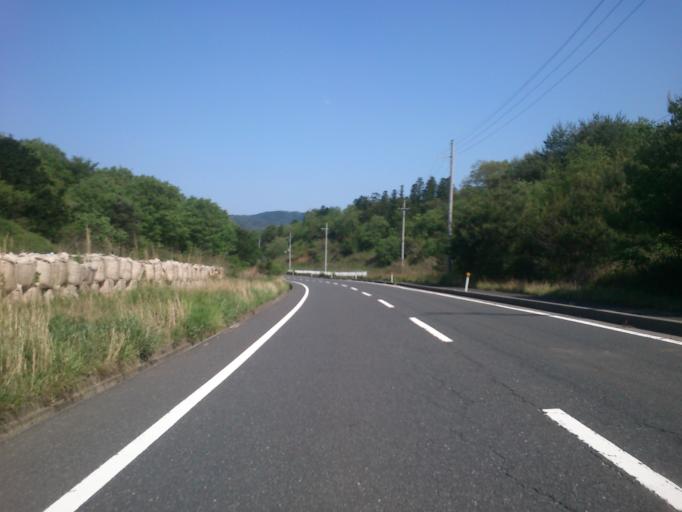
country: JP
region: Kyoto
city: Miyazu
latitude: 35.6655
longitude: 135.1022
